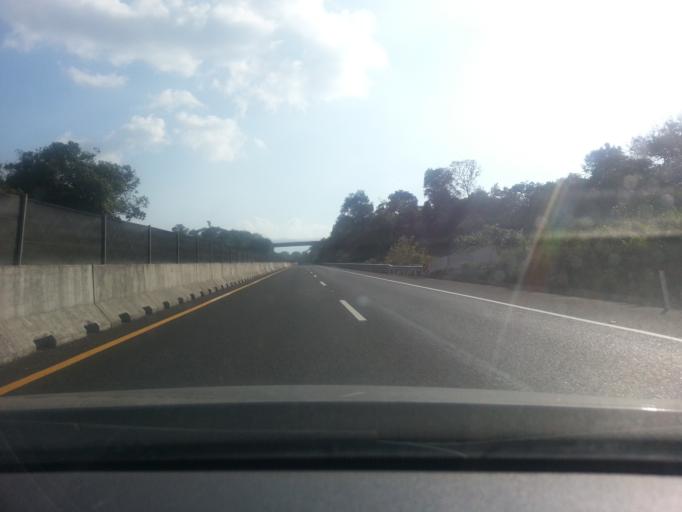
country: MX
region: Puebla
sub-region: Xicotepec
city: San Lorenzo
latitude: 20.4281
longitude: -97.9211
